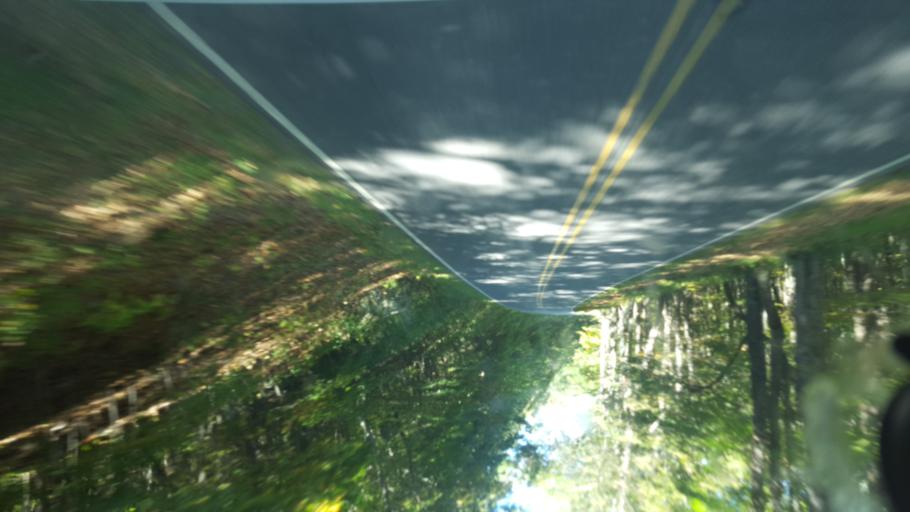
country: US
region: Virginia
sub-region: Page County
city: Stanley
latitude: 38.4799
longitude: -78.4551
